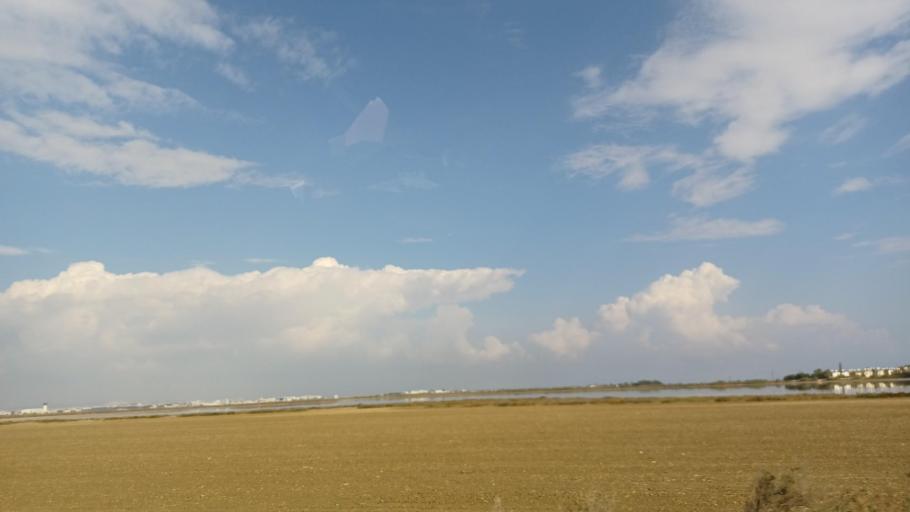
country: CY
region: Larnaka
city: Meneou
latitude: 34.8473
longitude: 33.6145
